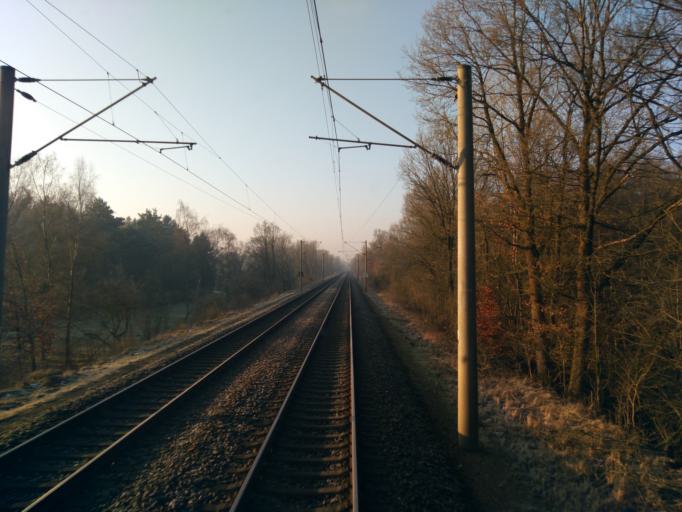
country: DE
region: Lower Saxony
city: Buchholz in der Nordheide
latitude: 53.3417
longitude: 9.9040
